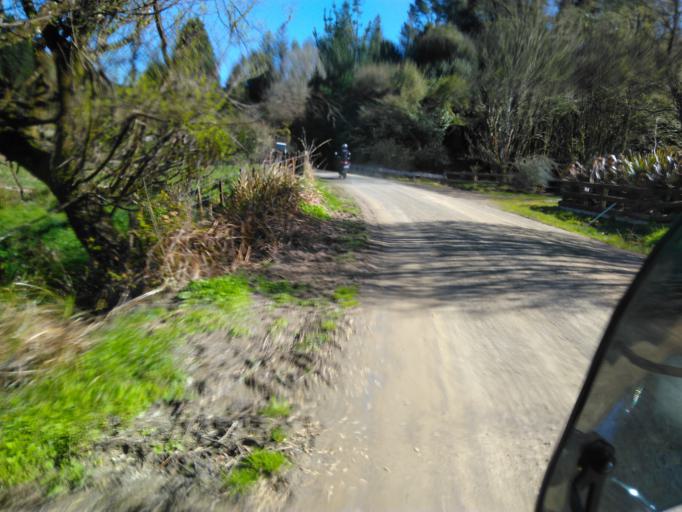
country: NZ
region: Bay of Plenty
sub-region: Opotiki District
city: Opotiki
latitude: -38.2954
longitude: 177.5524
